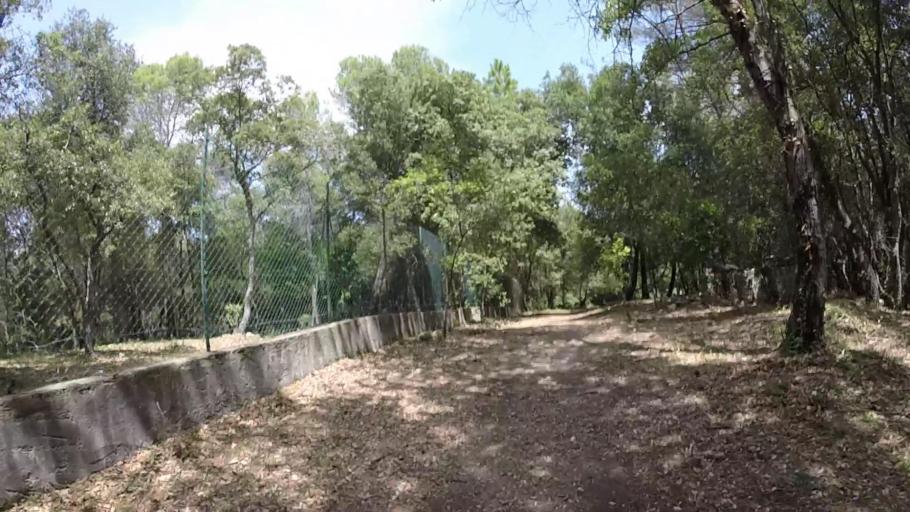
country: FR
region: Provence-Alpes-Cote d'Azur
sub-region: Departement des Alpes-Maritimes
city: Mougins
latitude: 43.6163
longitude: 7.0179
